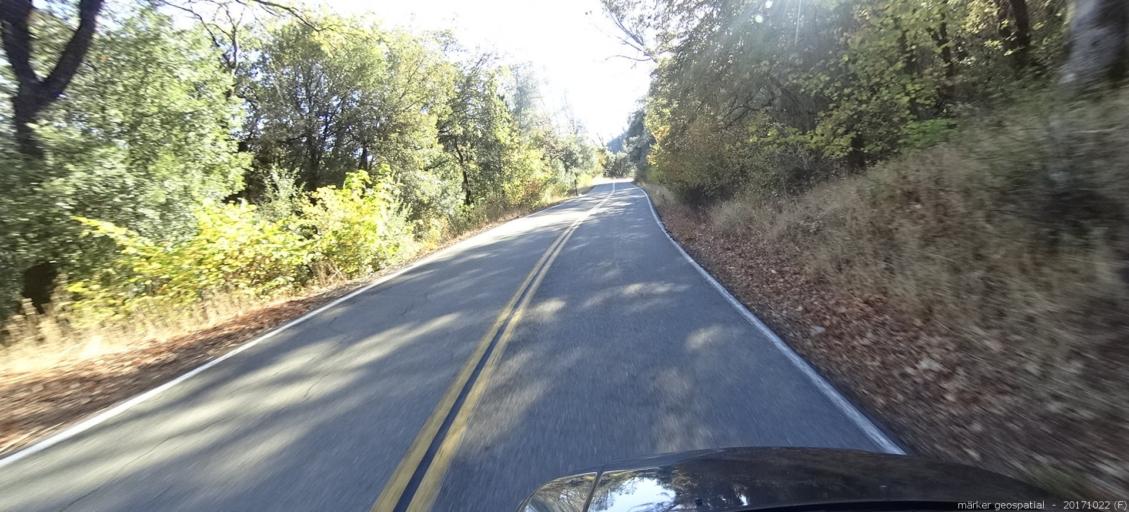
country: US
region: California
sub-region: Shasta County
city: Bella Vista
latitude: 40.8884
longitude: -122.2265
